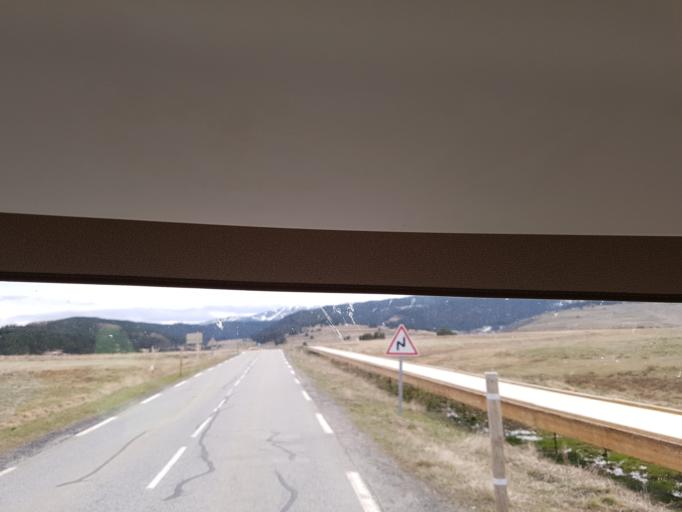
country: ES
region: Catalonia
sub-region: Provincia de Girona
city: Llivia
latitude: 42.6459
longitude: 2.1143
